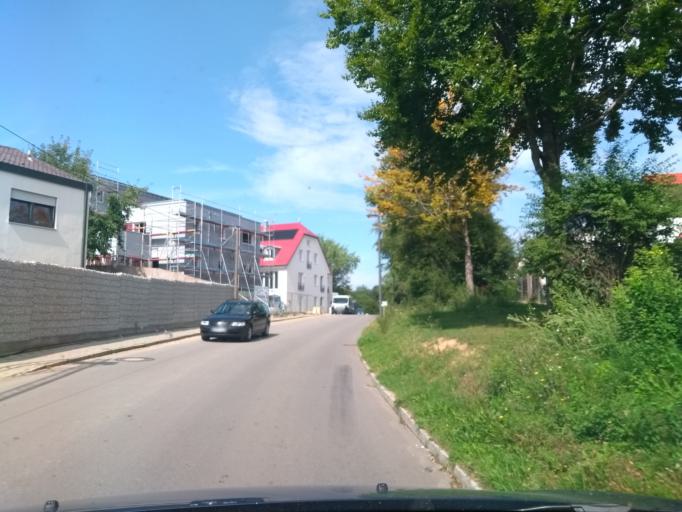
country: DE
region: Bavaria
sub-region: Upper Bavaria
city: Markt Indersdorf
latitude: 48.3658
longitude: 11.3774
